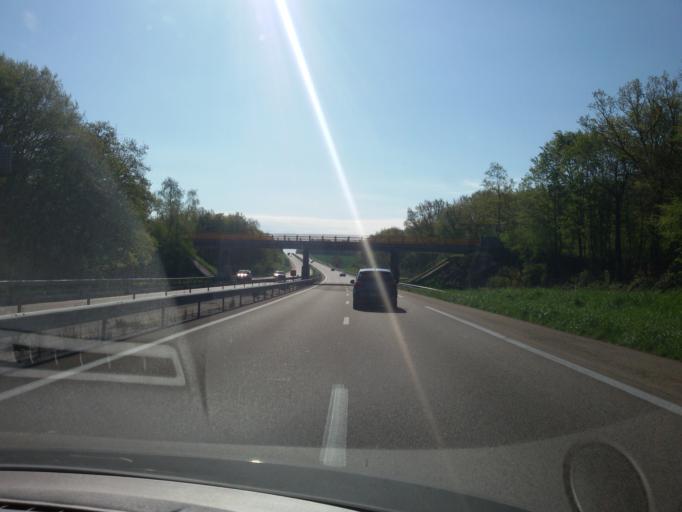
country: FR
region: Bourgogne
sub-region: Departement de l'Yonne
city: Vermenton
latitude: 47.7152
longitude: 3.7690
